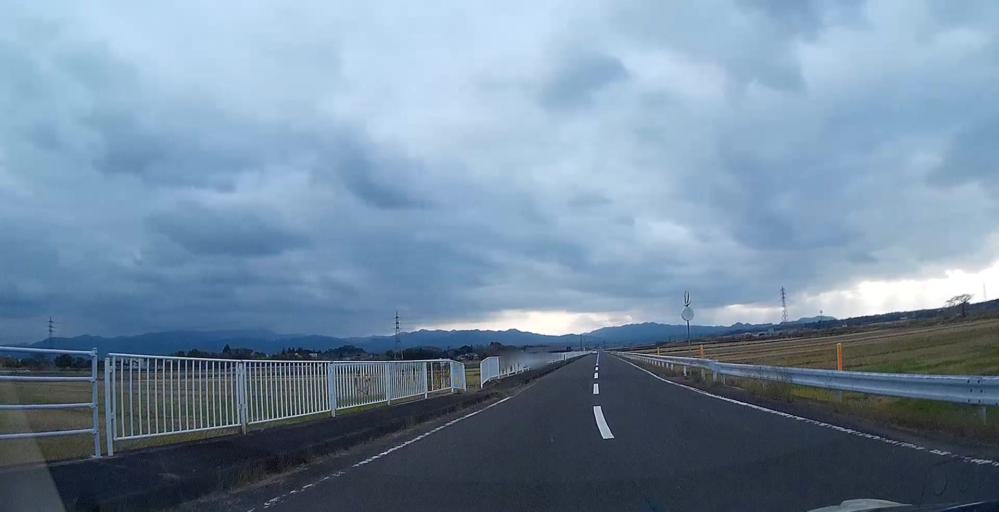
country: JP
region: Kagoshima
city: Izumi
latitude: 32.0910
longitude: 130.2755
